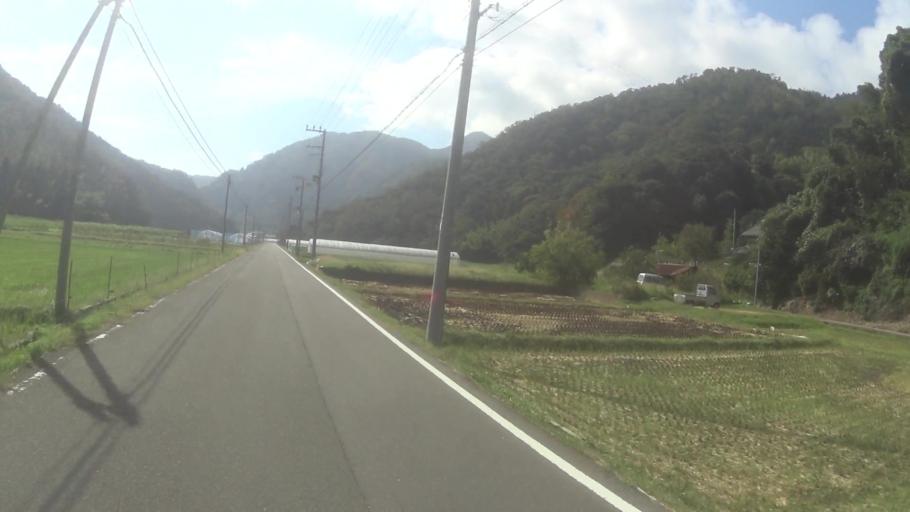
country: JP
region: Kyoto
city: Miyazu
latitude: 35.7416
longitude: 135.1613
